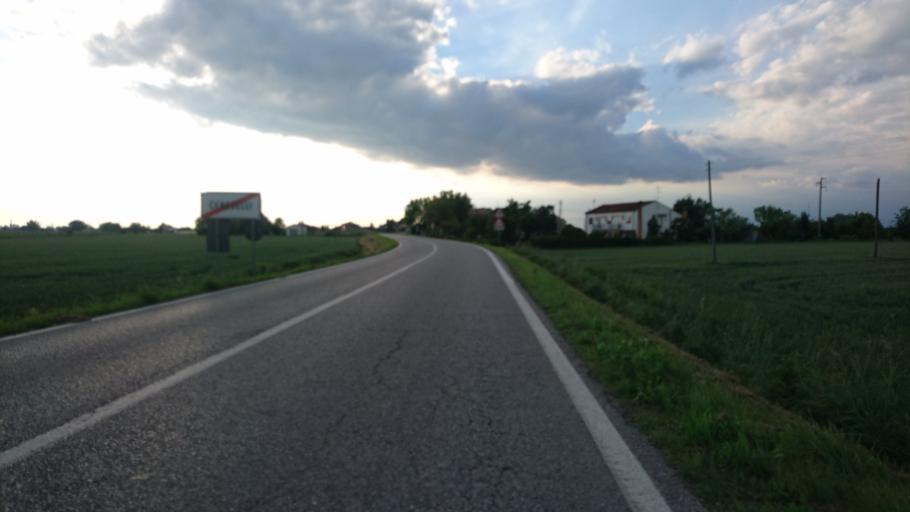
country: IT
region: Veneto
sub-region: Provincia di Rovigo
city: Ceneselli
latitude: 45.0184
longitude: 11.3617
